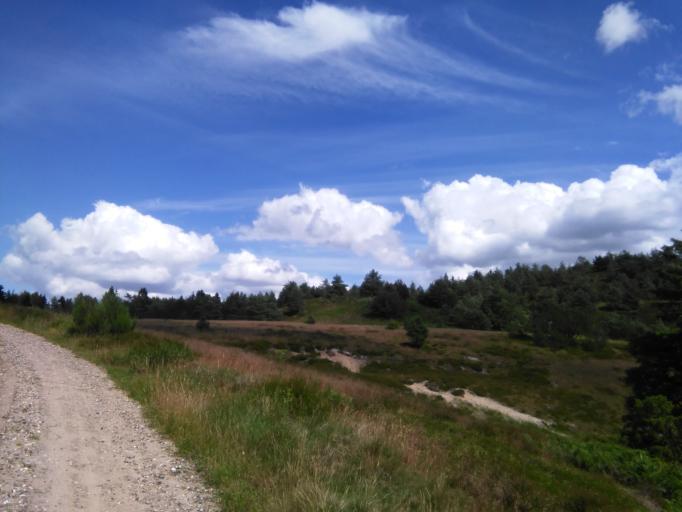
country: DK
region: Central Jutland
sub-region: Silkeborg Kommune
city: Virklund
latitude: 56.0720
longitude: 9.4520
